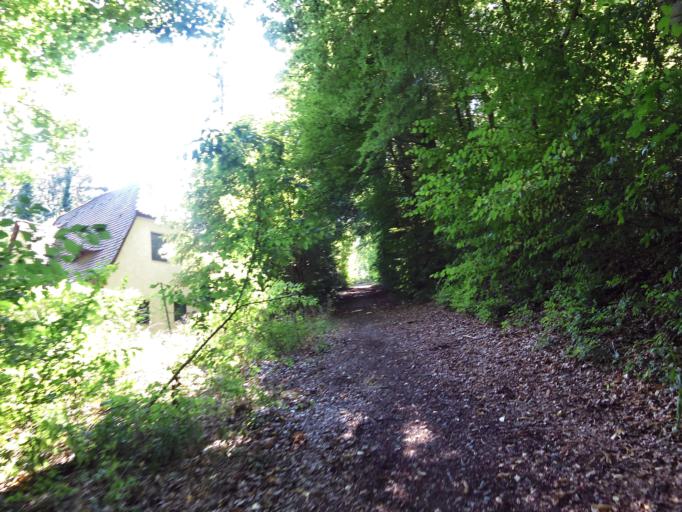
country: DE
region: Bavaria
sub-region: Regierungsbezirk Unterfranken
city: Hochberg
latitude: 49.7699
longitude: 9.9121
